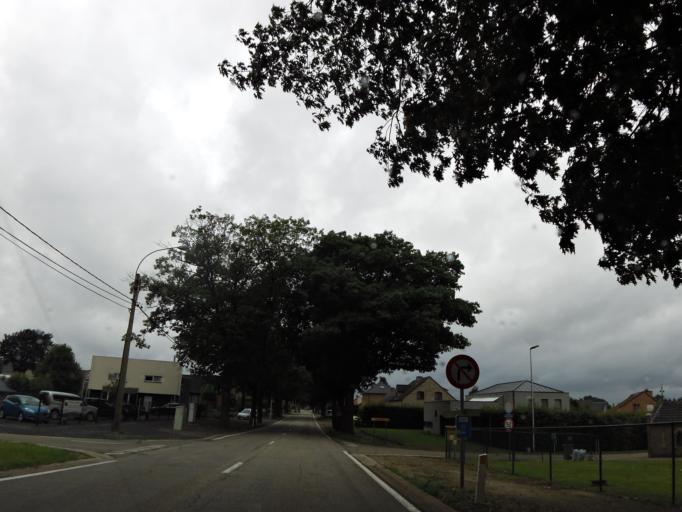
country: BE
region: Flanders
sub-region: Provincie Limburg
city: Bree
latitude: 51.0885
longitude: 5.6189
